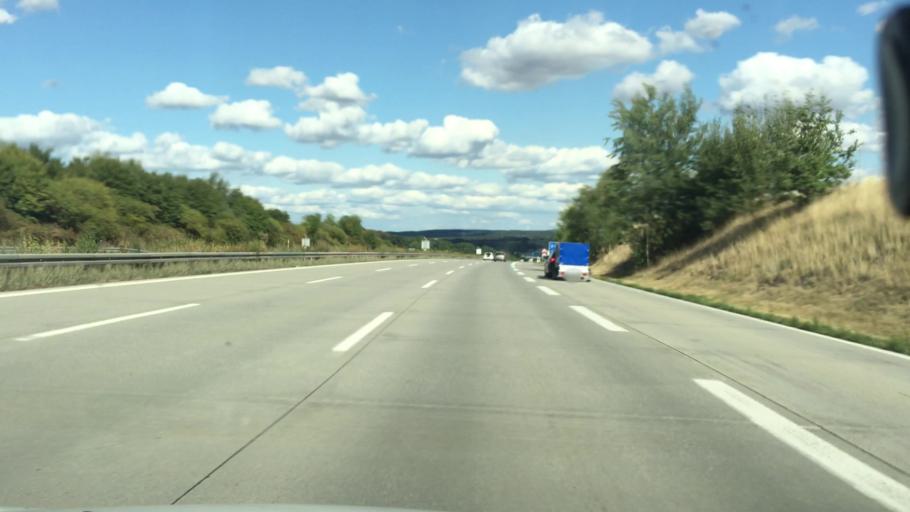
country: DE
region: Saxony
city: Pfaffroda
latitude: 50.8400
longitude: 12.5056
